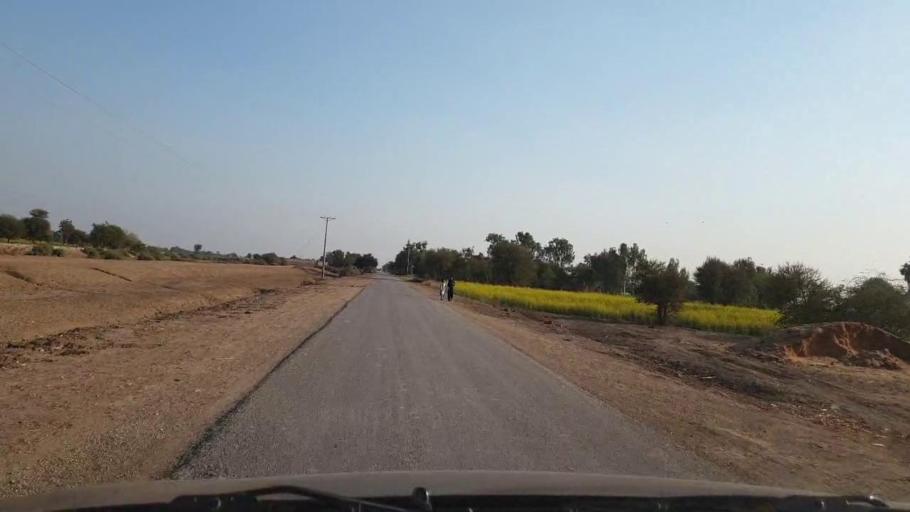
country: PK
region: Sindh
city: Jhol
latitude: 25.9550
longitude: 68.8984
